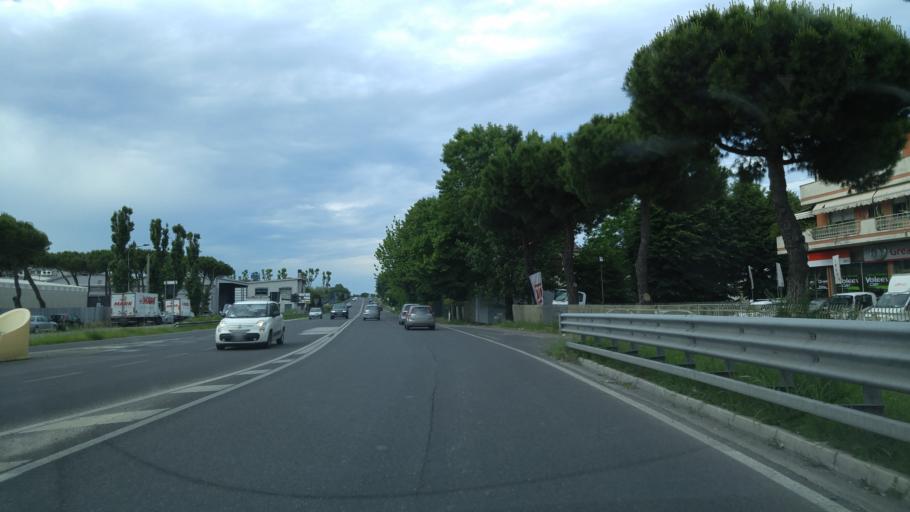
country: IT
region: Emilia-Romagna
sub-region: Provincia di Rimini
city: Rimini
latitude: 44.0646
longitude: 12.5416
